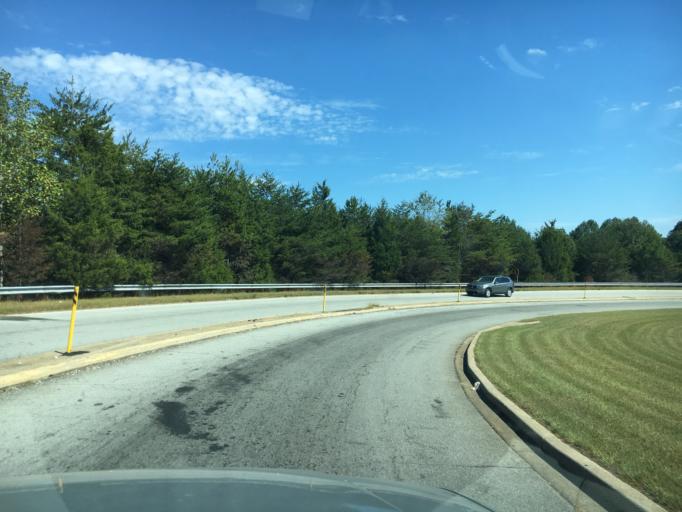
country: US
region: South Carolina
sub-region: Anderson County
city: Powdersville
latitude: 34.8300
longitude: -82.5290
